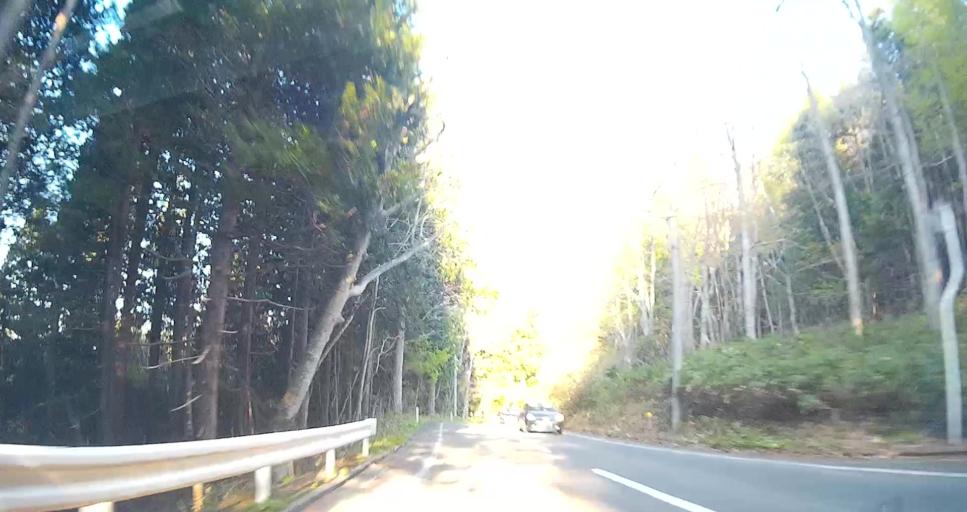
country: JP
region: Aomori
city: Mutsu
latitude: 41.3152
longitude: 141.1228
